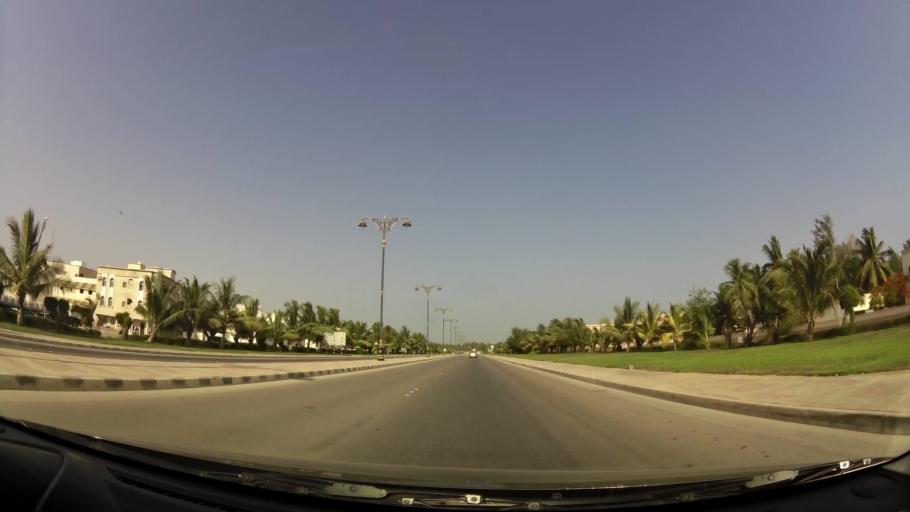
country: OM
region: Zufar
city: Salalah
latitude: 17.0036
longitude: 54.0618
